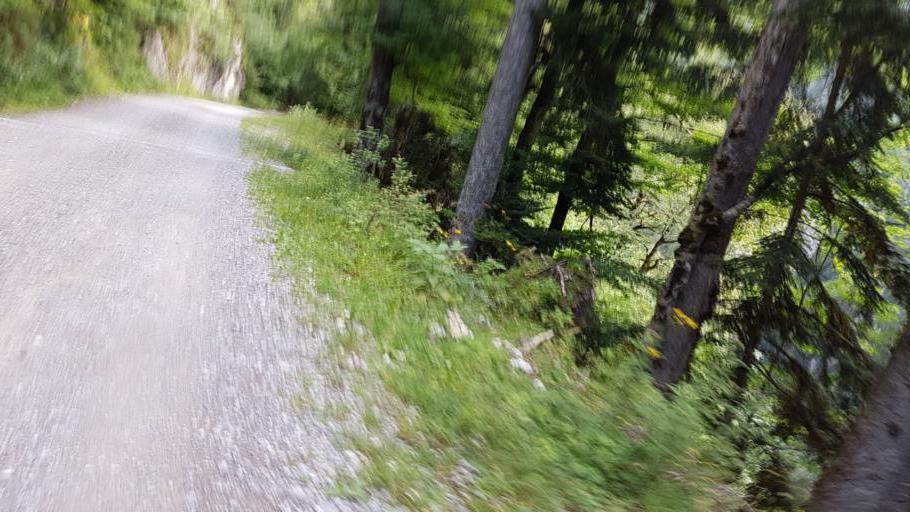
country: CH
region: Bern
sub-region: Obersimmental-Saanen District
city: Boltigen
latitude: 46.6706
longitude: 7.4617
